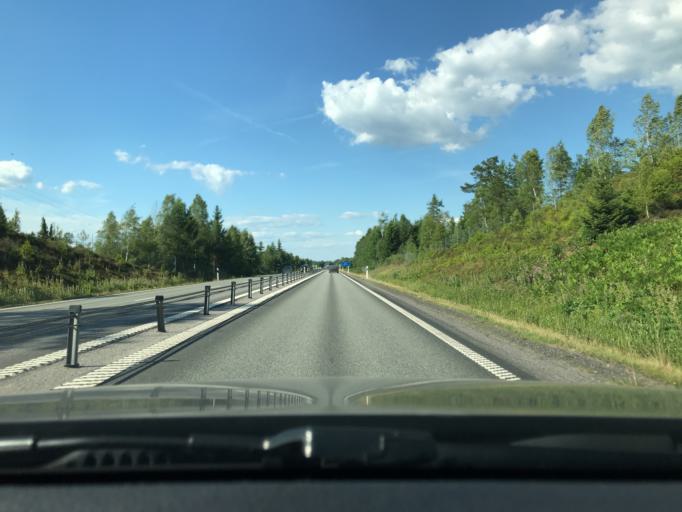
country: SE
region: Kronoberg
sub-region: Almhults Kommun
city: AElmhult
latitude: 56.4926
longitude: 14.1180
